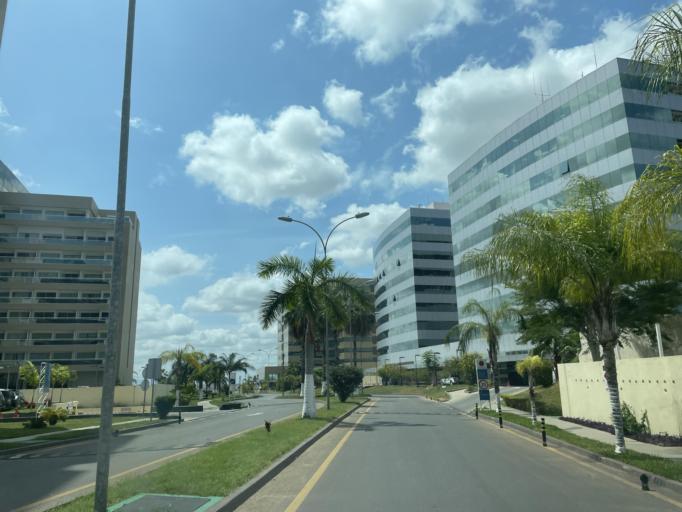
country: AO
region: Luanda
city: Luanda
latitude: -8.9228
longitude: 13.1889
